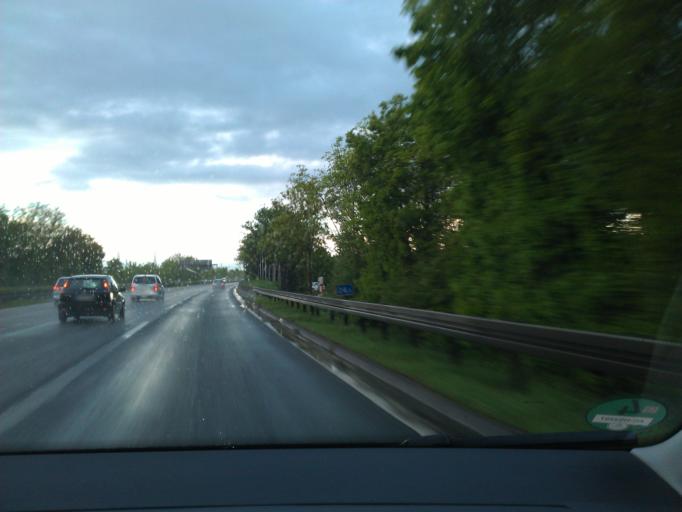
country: DE
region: North Rhine-Westphalia
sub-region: Regierungsbezirk Koln
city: Troisdorf
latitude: 50.7821
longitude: 7.1499
